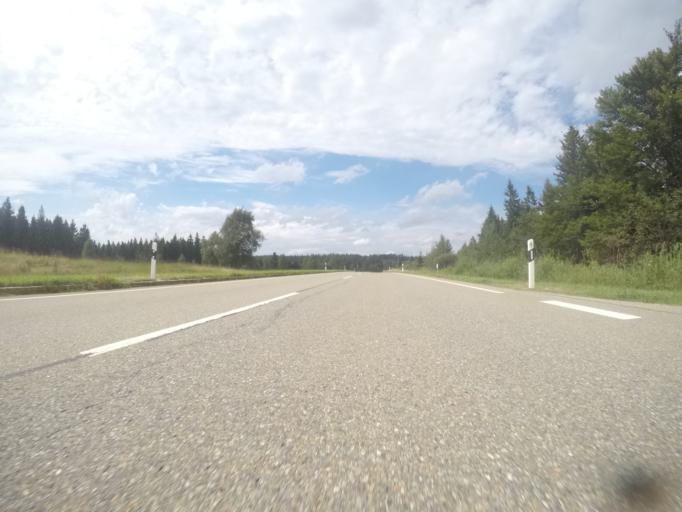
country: DE
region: Baden-Wuerttemberg
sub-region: Freiburg Region
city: Bad Peterstal-Griesbach
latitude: 48.4881
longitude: 8.2720
